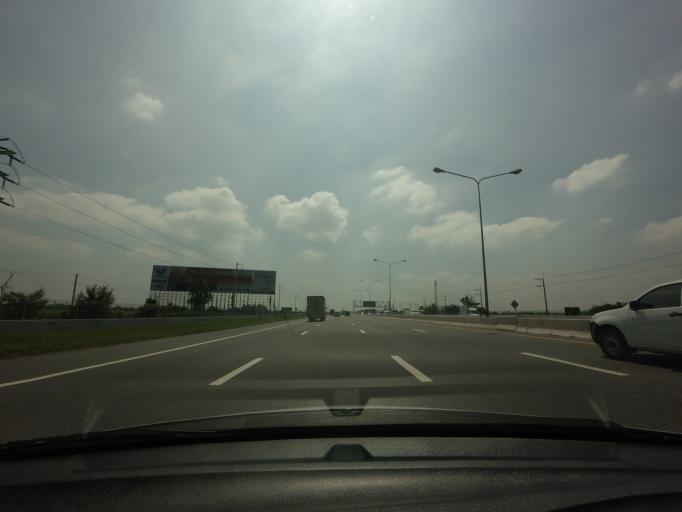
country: TH
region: Chachoengsao
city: Bang Pakong
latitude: 13.5902
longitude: 100.9665
